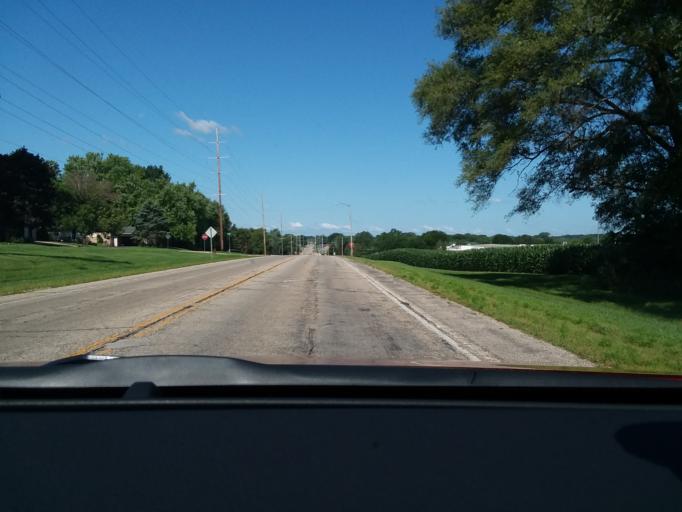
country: US
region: Wisconsin
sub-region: Dane County
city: De Forest
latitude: 43.2529
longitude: -89.3307
